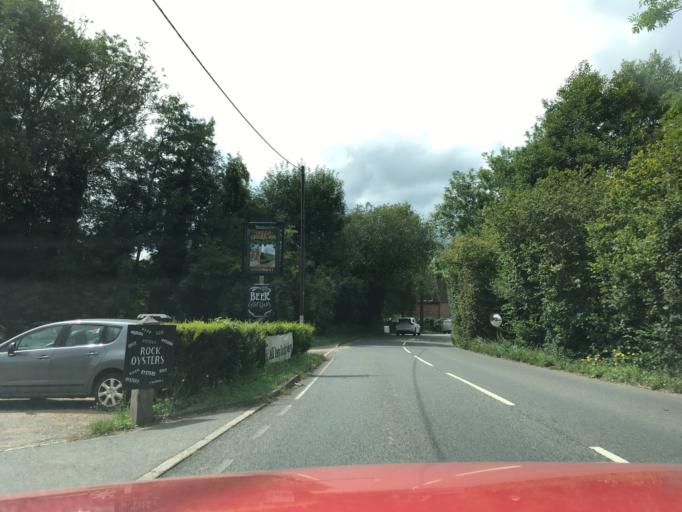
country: GB
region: England
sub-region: Kent
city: Marden
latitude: 51.1087
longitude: 0.4402
